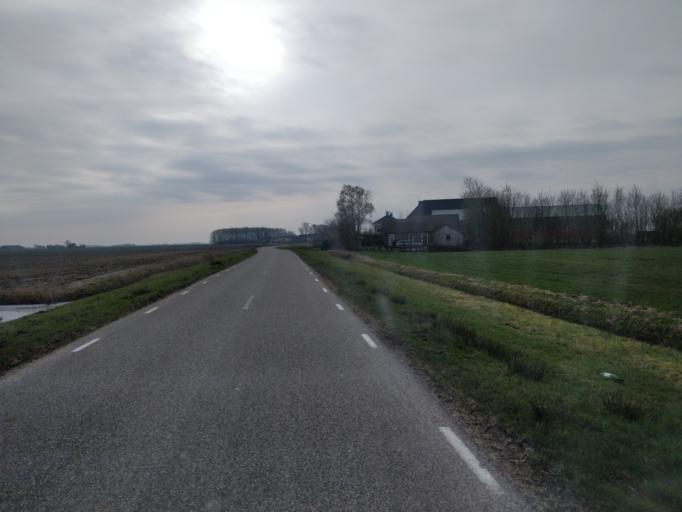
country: NL
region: Friesland
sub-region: Gemeente Dongeradeel
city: Ternaard
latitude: 53.3570
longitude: 5.9376
